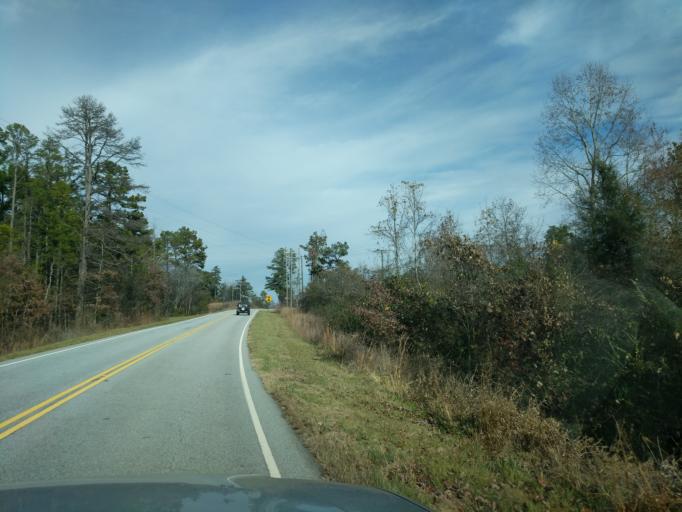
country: US
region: South Carolina
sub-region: Oconee County
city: Utica
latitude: 34.7828
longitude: -82.9058
